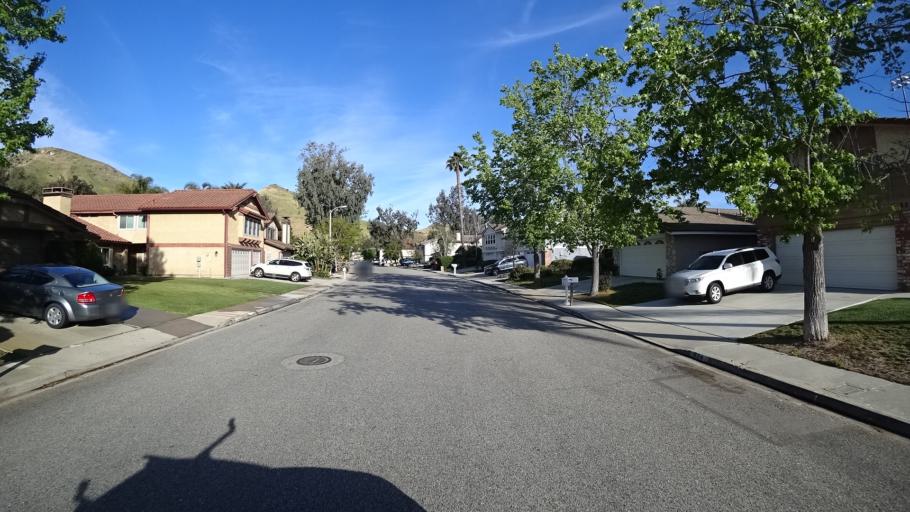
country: US
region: California
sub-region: Ventura County
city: Casa Conejo
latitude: 34.1905
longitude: -118.9564
